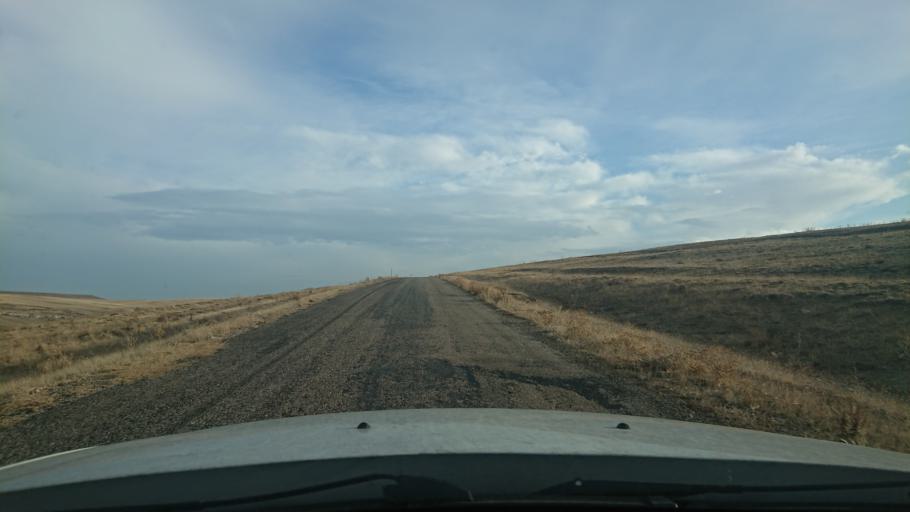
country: TR
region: Aksaray
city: Acipinar
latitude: 38.6575
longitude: 33.8373
